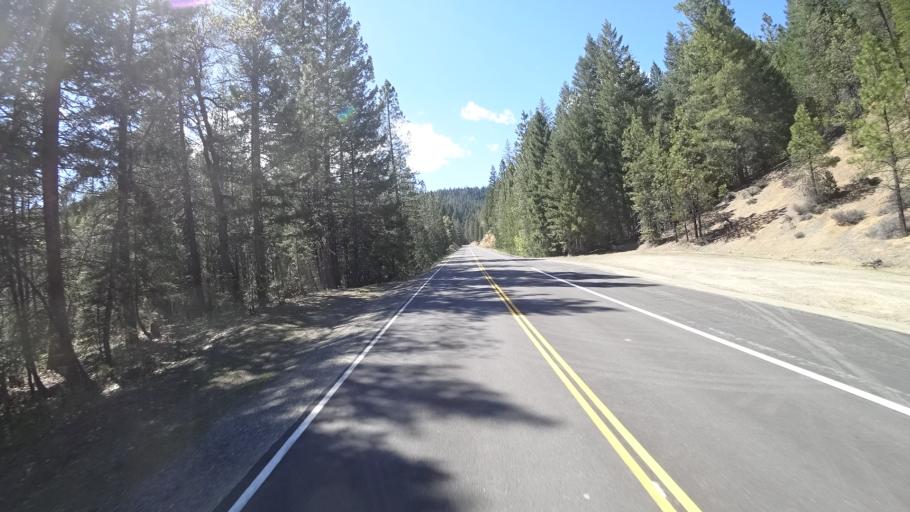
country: US
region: California
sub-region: Trinity County
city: Lewiston
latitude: 40.9050
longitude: -122.7817
